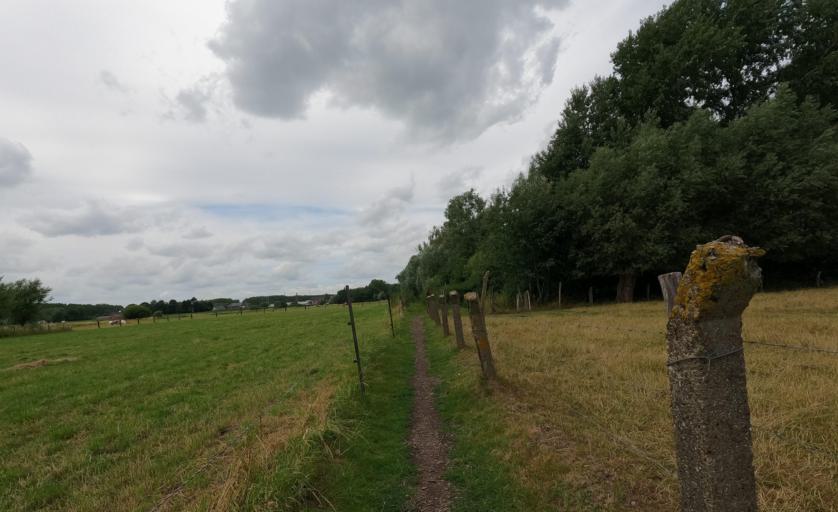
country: BE
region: Flanders
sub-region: Provincie Oost-Vlaanderen
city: Dendermonde
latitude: 51.0136
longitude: 4.1016
